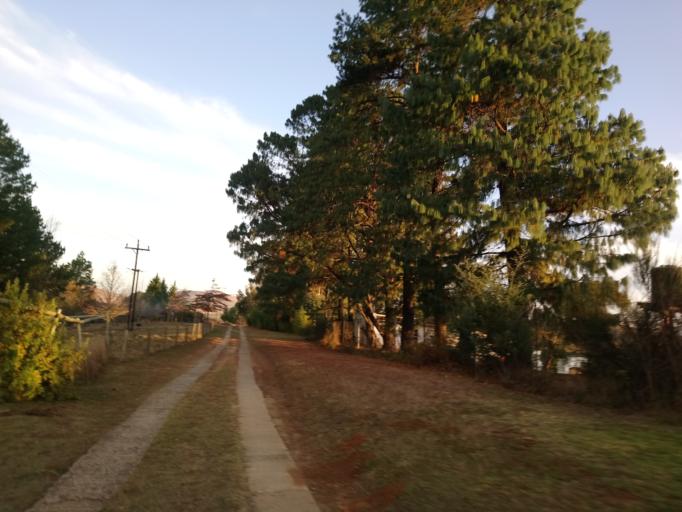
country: ZA
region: KwaZulu-Natal
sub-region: uMgungundlovu District Municipality
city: Mooirivier
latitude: -29.3328
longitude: 29.9195
